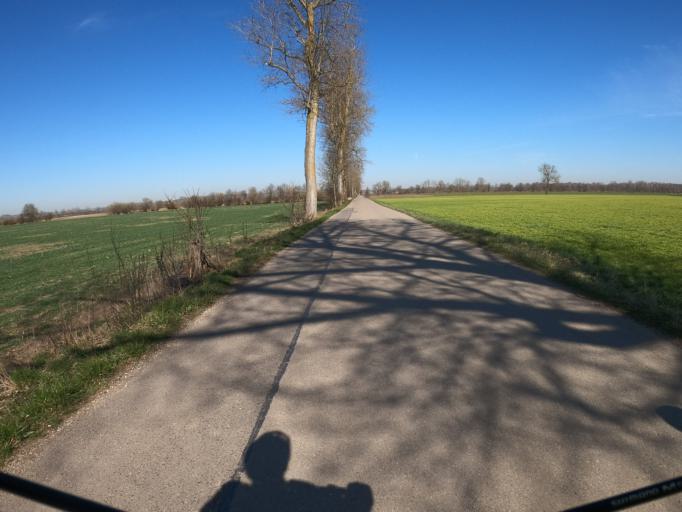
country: DE
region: Bavaria
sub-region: Swabia
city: Nersingen
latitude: 48.4637
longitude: 10.1443
